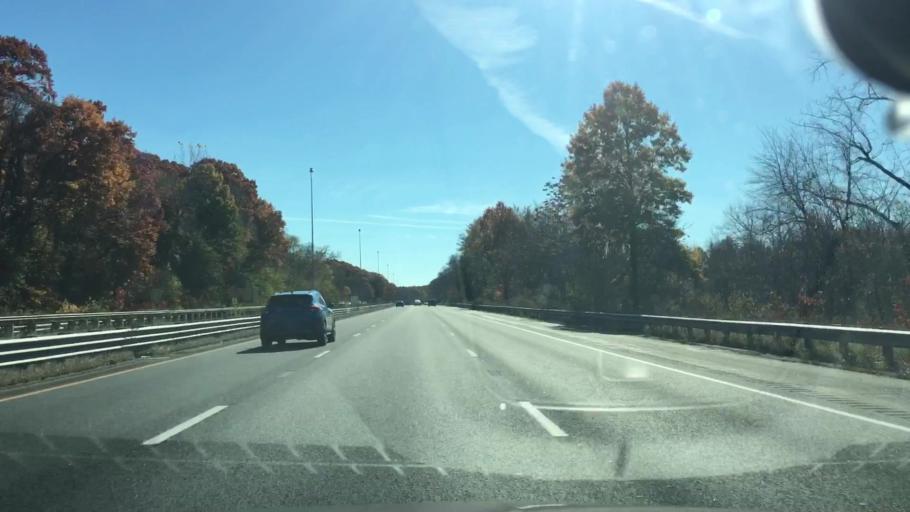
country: US
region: Massachusetts
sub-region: Hampden County
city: Longmeadow
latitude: 42.0480
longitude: -72.5892
